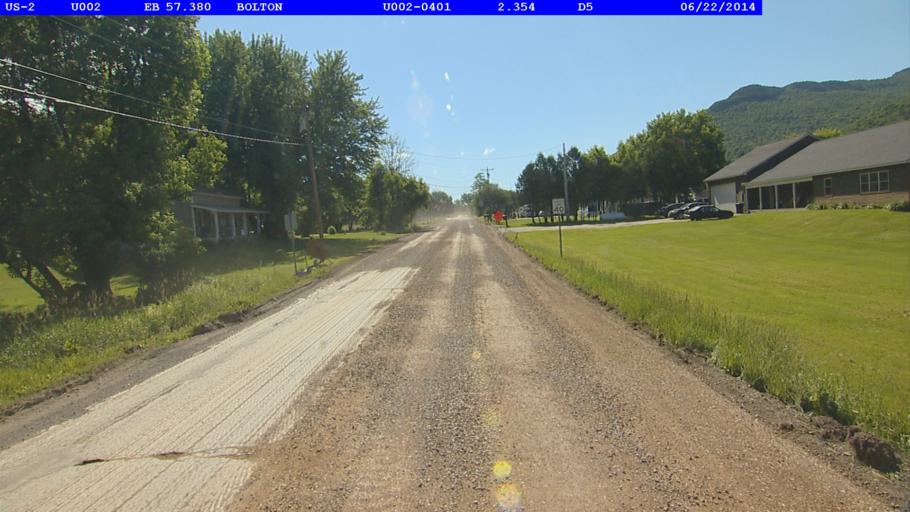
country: US
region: Vermont
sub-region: Washington County
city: Waterbury
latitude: 44.3745
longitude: -72.8880
